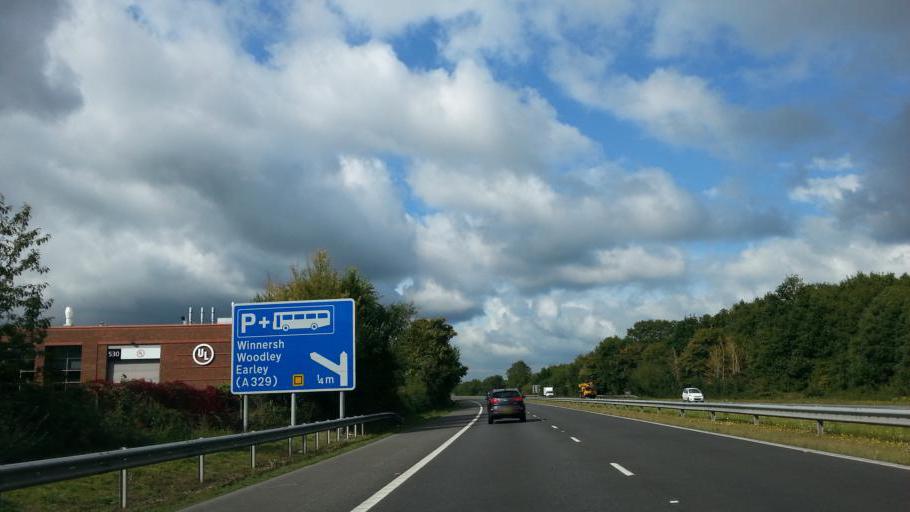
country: GB
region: England
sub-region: Wokingham
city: Woodley
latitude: 51.4394
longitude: -0.8794
